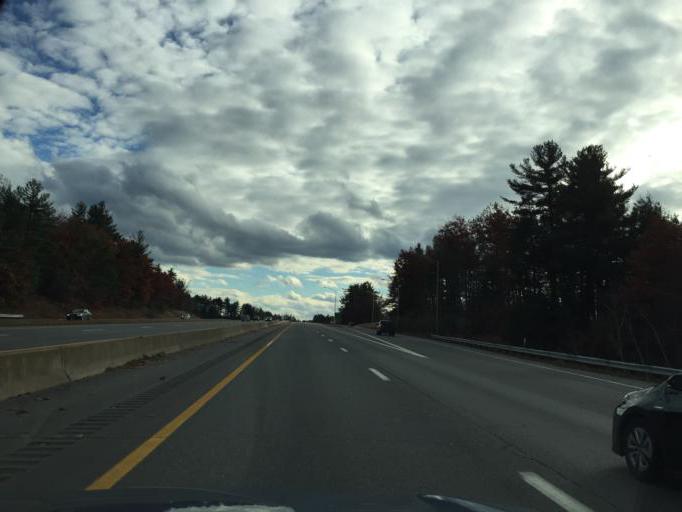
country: US
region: New Hampshire
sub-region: Hillsborough County
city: Litchfield
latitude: 42.8439
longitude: -71.4955
